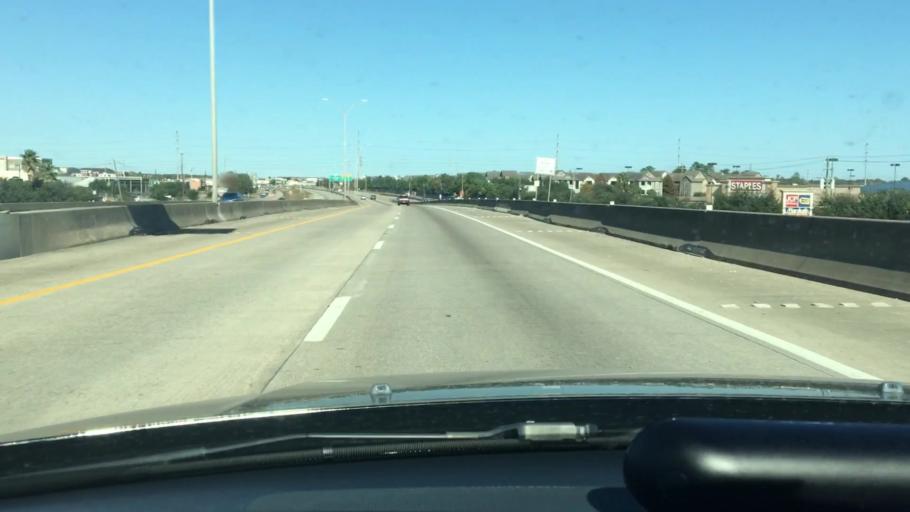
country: US
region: Texas
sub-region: Harris County
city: Cloverleaf
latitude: 29.8097
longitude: -95.1633
